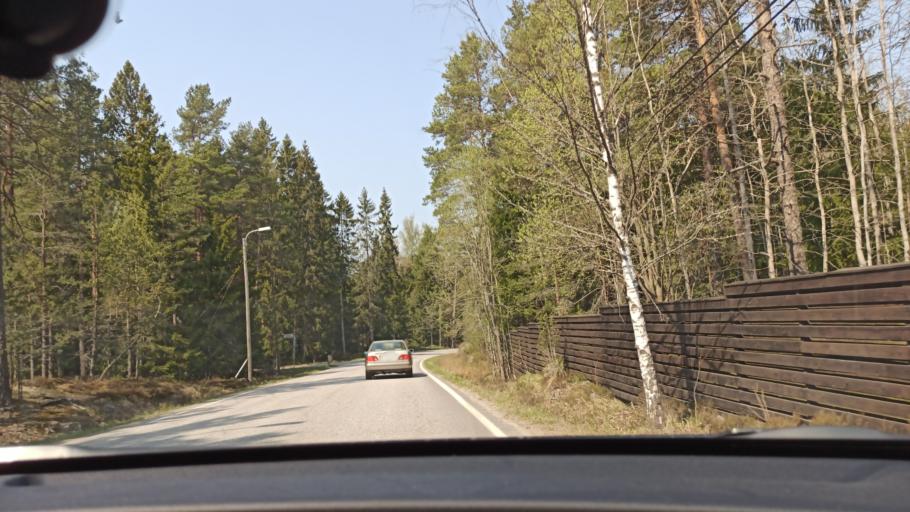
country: FI
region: Uusimaa
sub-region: Helsinki
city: Kirkkonummi
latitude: 60.0957
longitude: 24.5678
